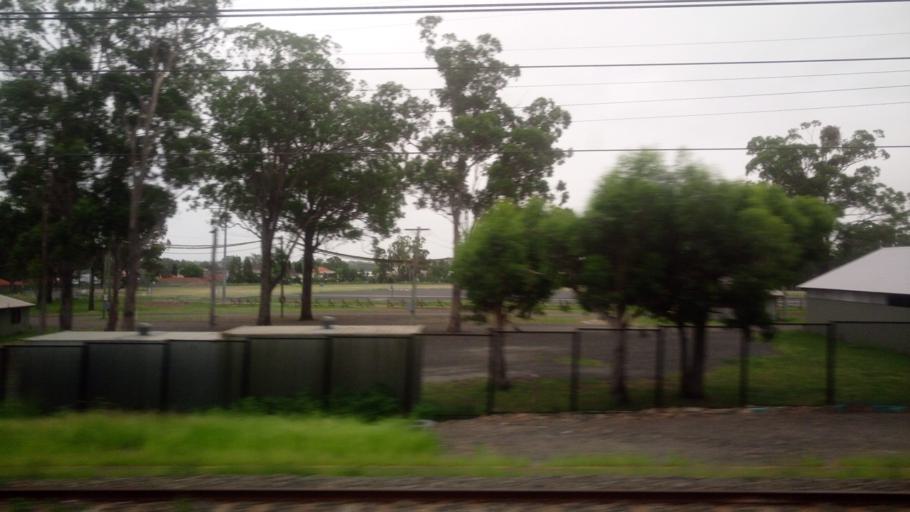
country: AU
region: New South Wales
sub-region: Blacktown
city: Blacktown
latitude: -33.7672
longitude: 150.9002
